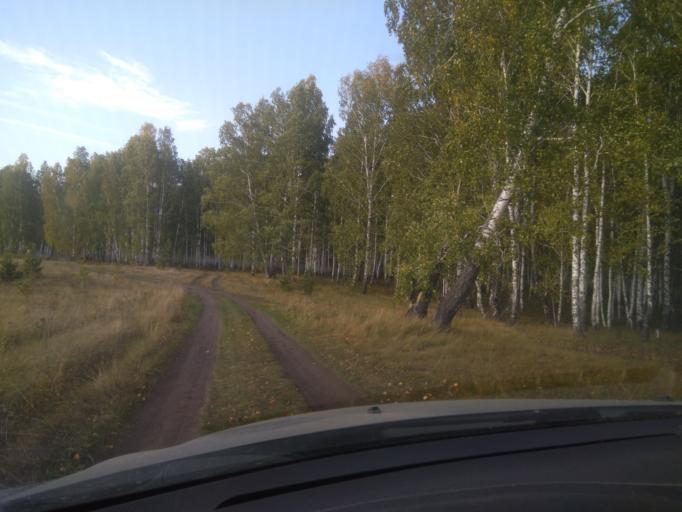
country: RU
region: Sverdlovsk
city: Pokrovskoye
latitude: 56.4291
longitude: 61.6096
